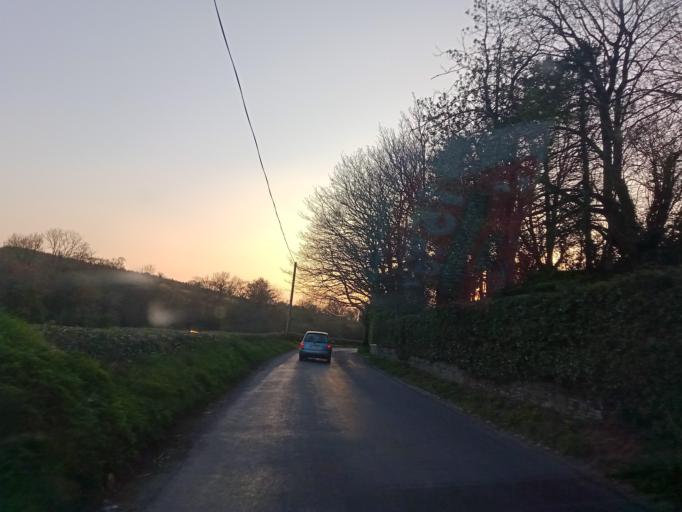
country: IE
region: Leinster
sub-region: Laois
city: Abbeyleix
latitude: 52.8623
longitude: -7.2782
